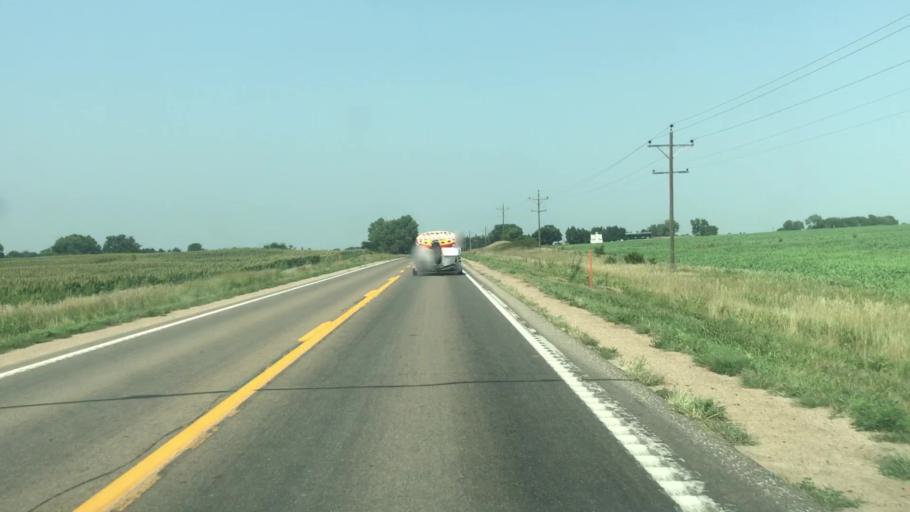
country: US
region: Nebraska
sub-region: Hall County
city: Wood River
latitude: 41.0146
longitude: -98.6073
